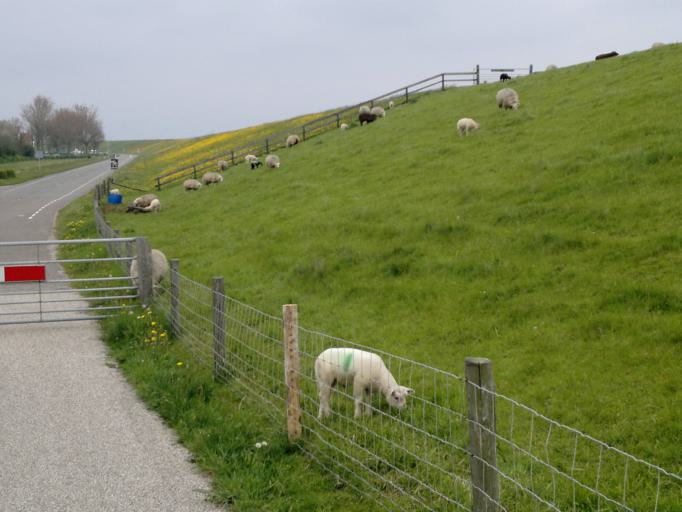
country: NL
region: North Holland
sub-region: Gemeente Texel
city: Den Burg
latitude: 53.0319
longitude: 4.8402
